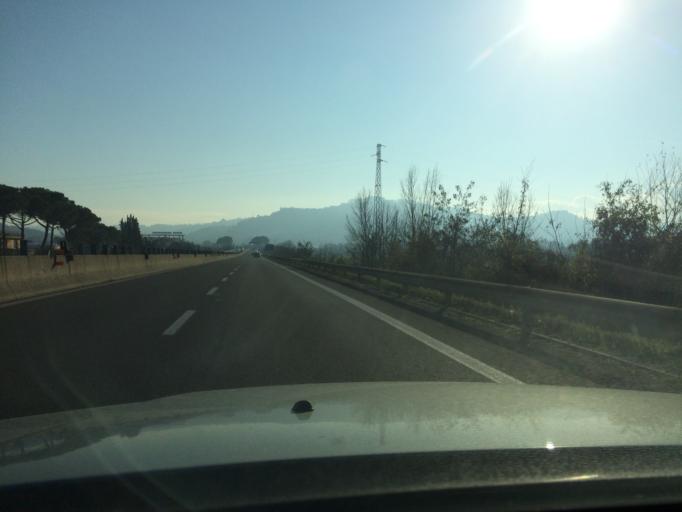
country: IT
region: Umbria
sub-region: Provincia di Perugia
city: Ponterio-Pian di Porto
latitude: 42.8108
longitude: 12.4059
